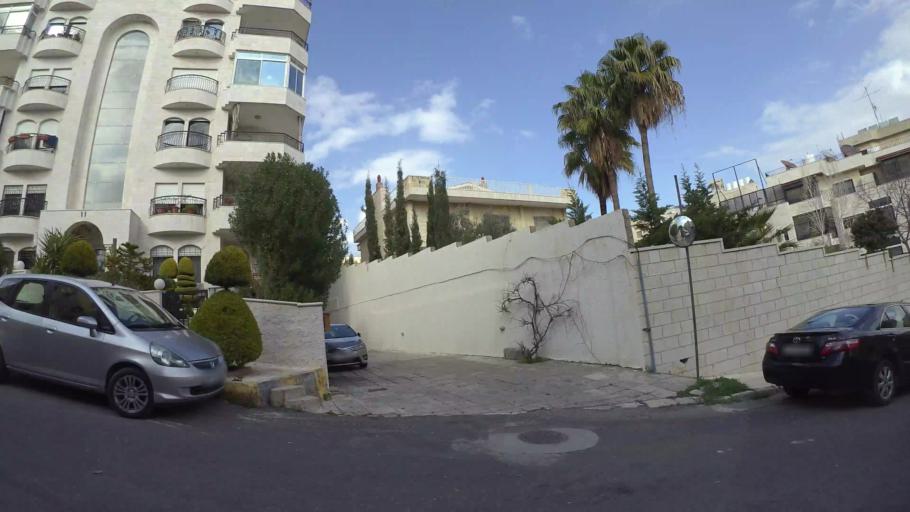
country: JO
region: Amman
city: Amman
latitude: 31.9617
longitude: 35.8921
